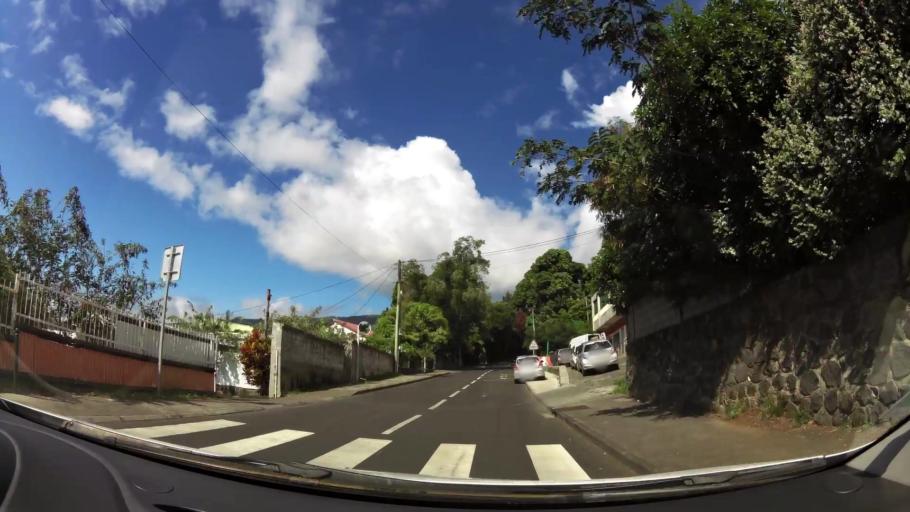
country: RE
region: Reunion
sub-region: Reunion
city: Saint-Denis
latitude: -20.9241
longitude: 55.4947
